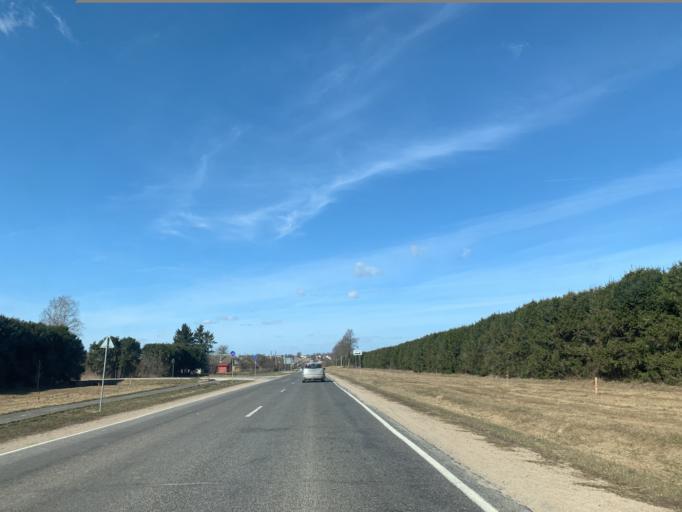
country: BY
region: Minsk
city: Haradzyeya
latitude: 53.2961
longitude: 26.5724
